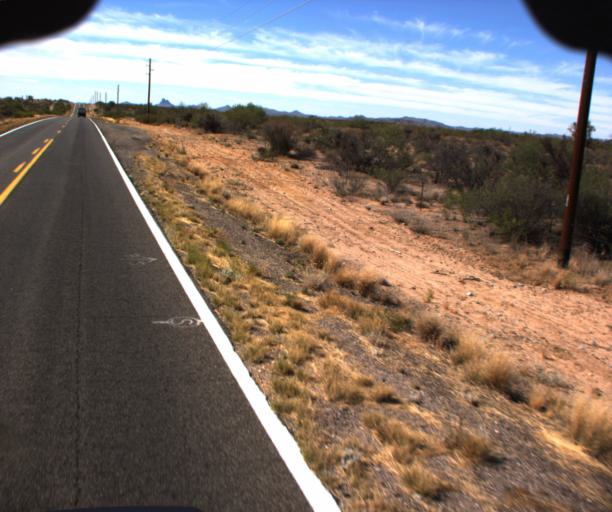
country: US
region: Arizona
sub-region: Yavapai County
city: Congress
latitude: 34.0687
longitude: -112.8210
